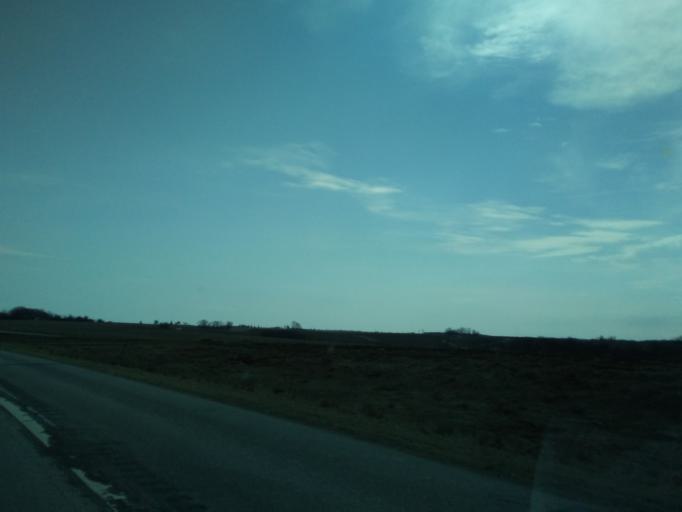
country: US
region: Minnesota
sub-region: Fillmore County
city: Harmony
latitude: 43.6153
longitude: -92.0183
